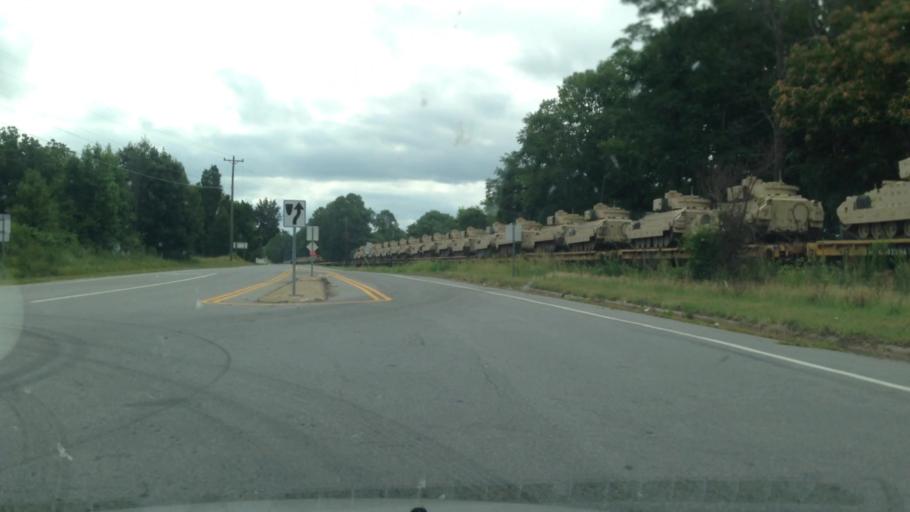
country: US
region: North Carolina
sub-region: Rockingham County
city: Reidsville
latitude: 36.4348
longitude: -79.5710
